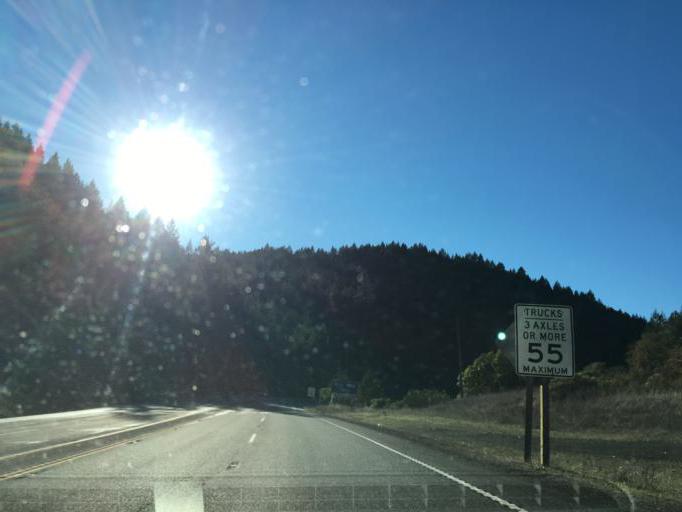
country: US
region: California
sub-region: Mendocino County
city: Laytonville
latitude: 39.8278
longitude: -123.5796
